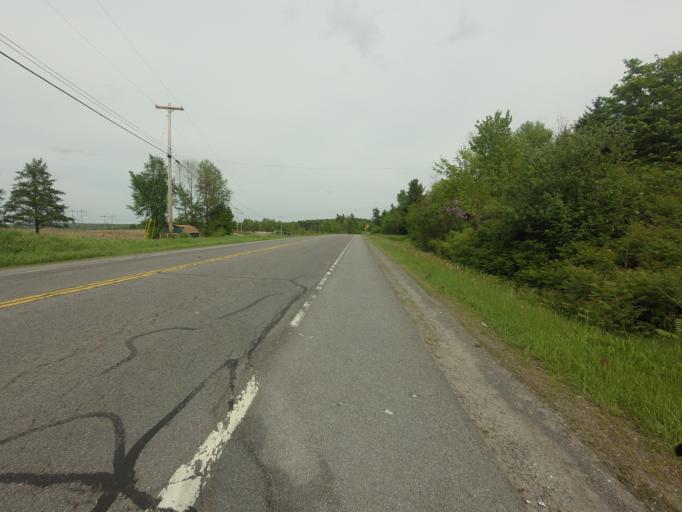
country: US
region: New York
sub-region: St. Lawrence County
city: Gouverneur
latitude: 44.3157
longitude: -75.2382
